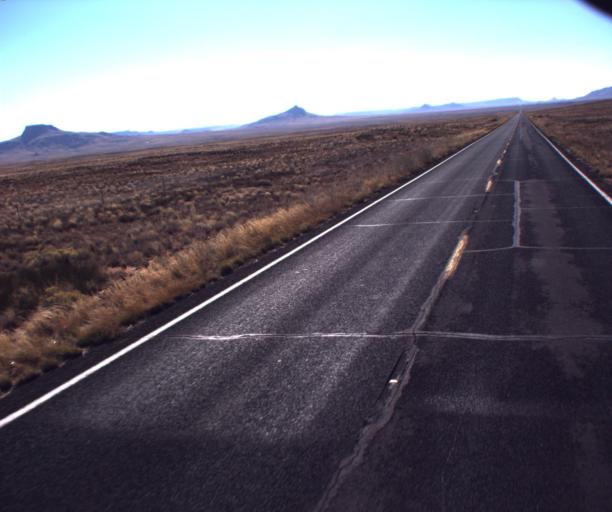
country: US
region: Arizona
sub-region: Navajo County
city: First Mesa
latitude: 35.6092
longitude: -110.4742
